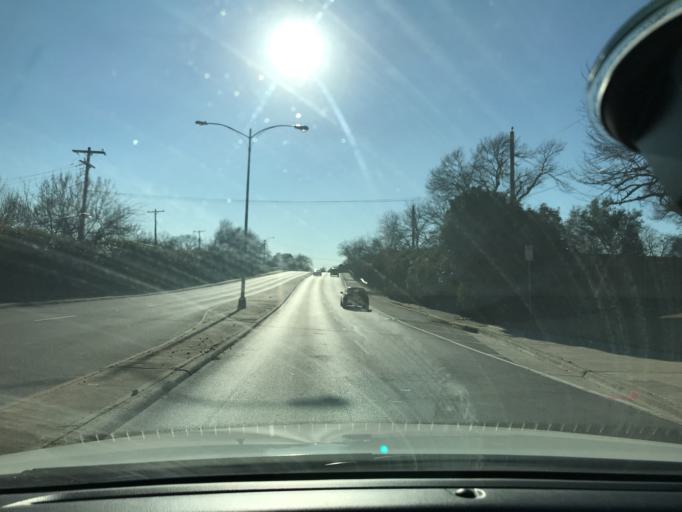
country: US
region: Texas
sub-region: Dallas County
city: Highland Park
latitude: 32.8457
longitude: -96.7376
